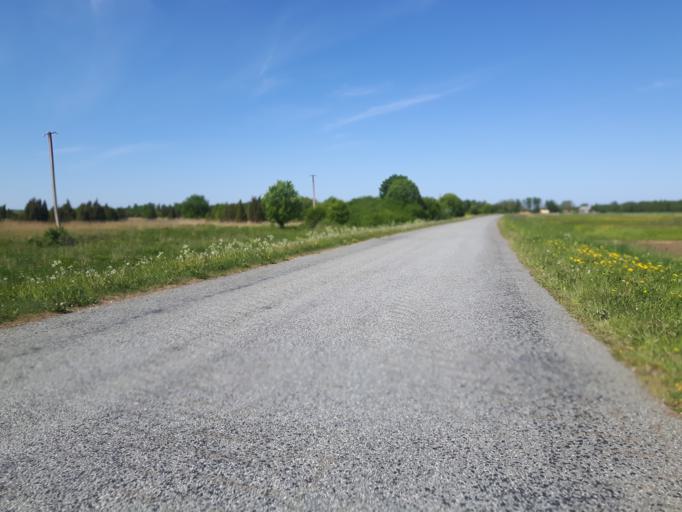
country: EE
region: Ida-Virumaa
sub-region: Aseri vald
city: Aseri
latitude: 59.4723
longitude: 26.8055
